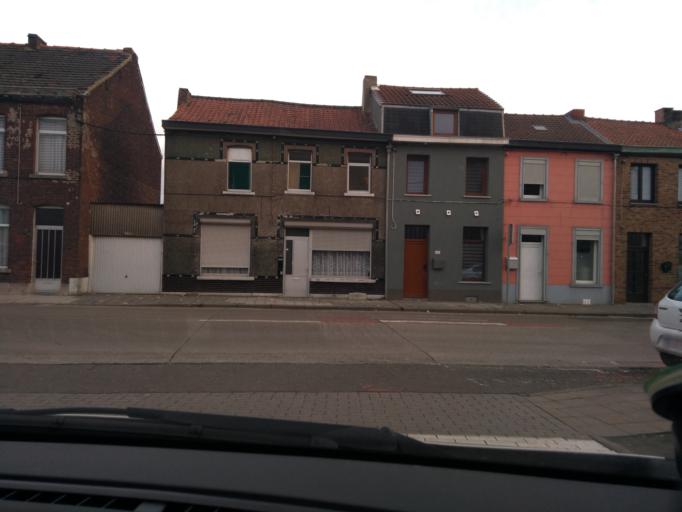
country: BE
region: Wallonia
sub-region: Province du Hainaut
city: Binche
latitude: 50.4190
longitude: 4.1698
